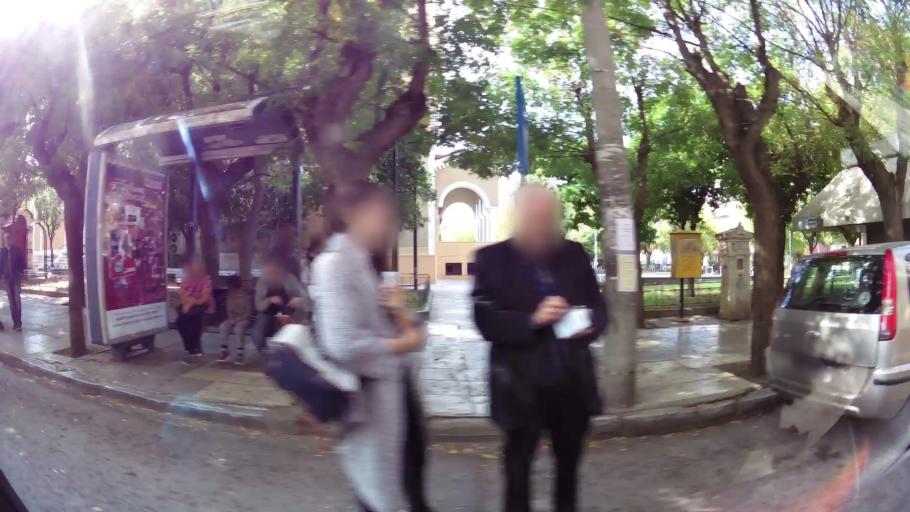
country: GR
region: Attica
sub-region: Nomarchia Athinas
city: Athens
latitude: 37.9876
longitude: 23.7127
